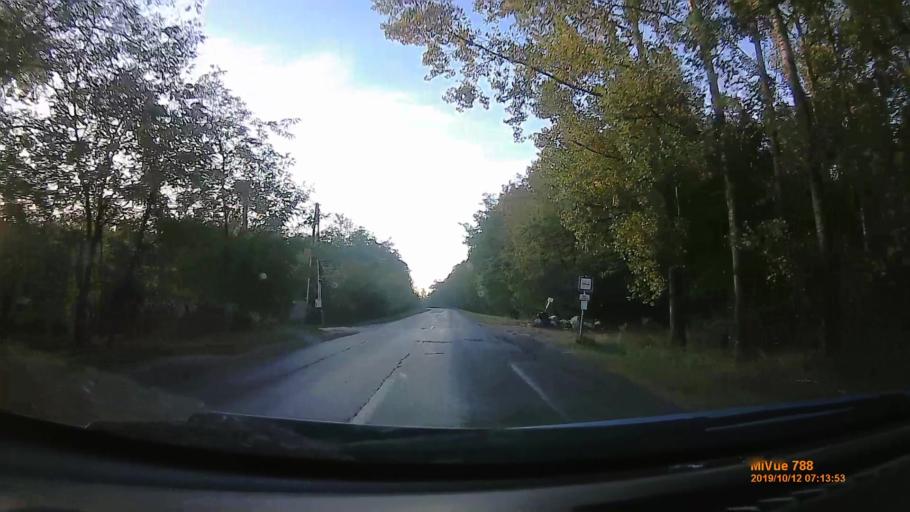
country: HU
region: Hajdu-Bihar
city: Hajdubagos
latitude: 47.4366
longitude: 21.6972
